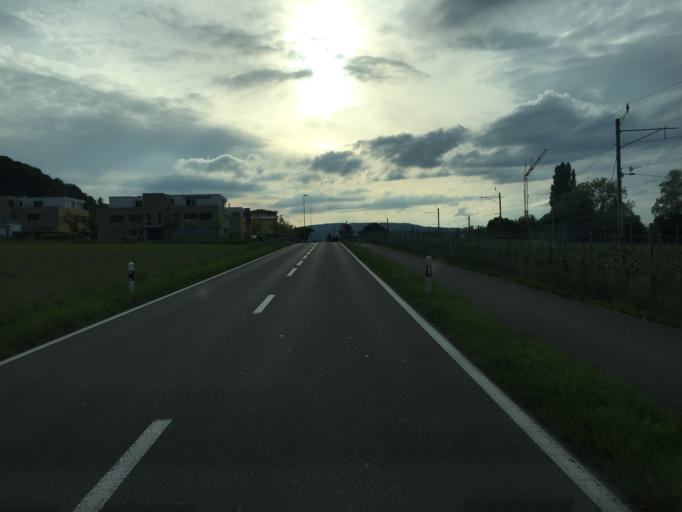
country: DE
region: Baden-Wuerttemberg
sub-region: Freiburg Region
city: Reichenau
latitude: 47.6733
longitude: 9.0388
